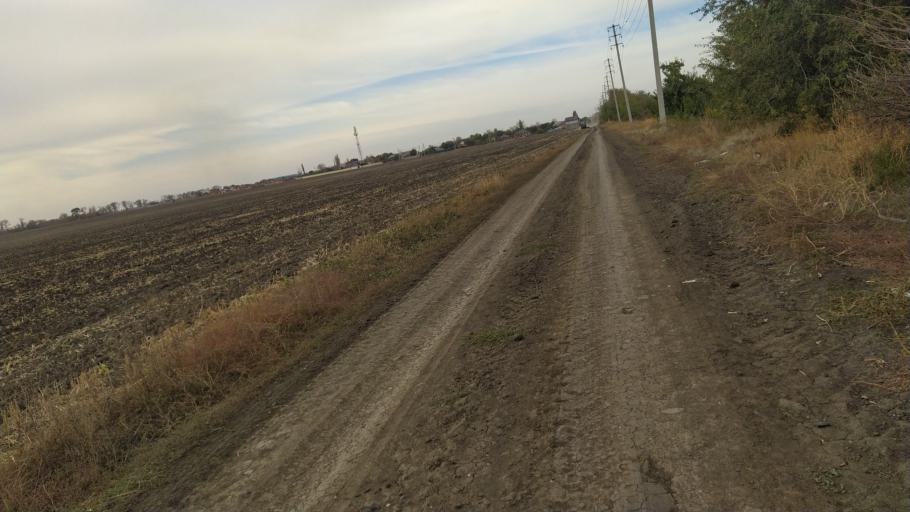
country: RU
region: Rostov
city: Bataysk
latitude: 47.1088
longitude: 39.6845
